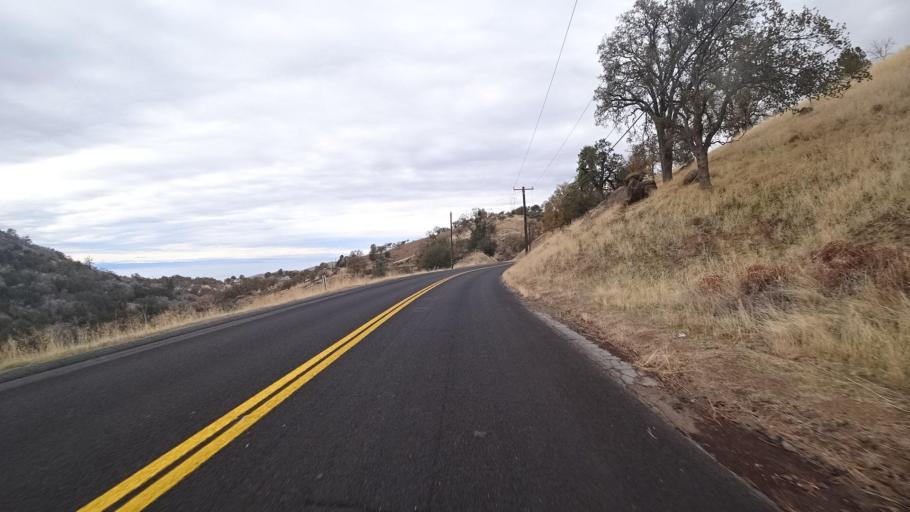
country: US
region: California
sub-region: Kern County
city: Stallion Springs
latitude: 35.0955
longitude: -118.6647
